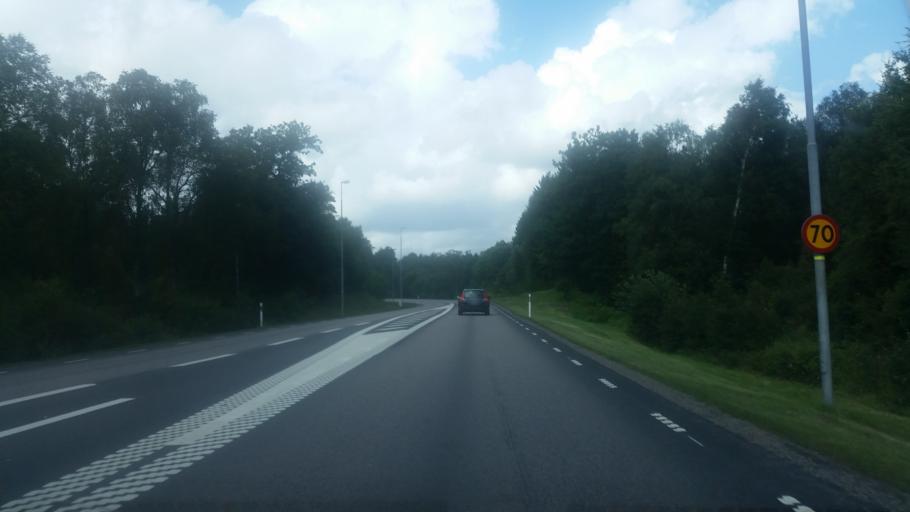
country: SE
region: Vaestra Goetaland
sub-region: Partille Kommun
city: Furulund
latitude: 57.7194
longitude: 12.1395
